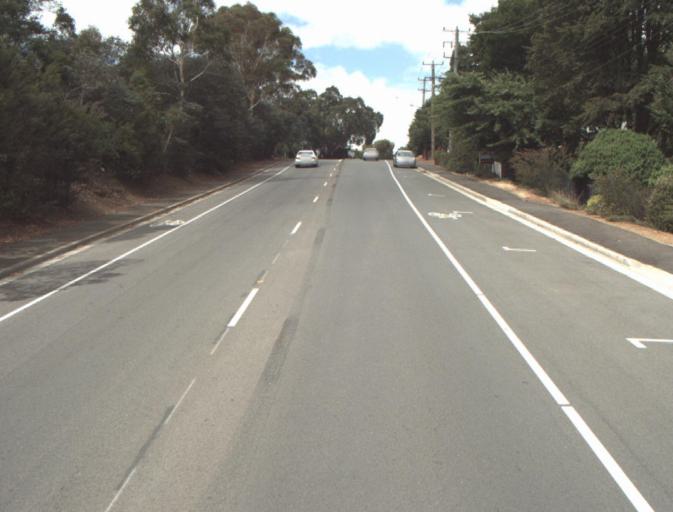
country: AU
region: Tasmania
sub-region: Launceston
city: Newstead
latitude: -41.4531
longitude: 147.1742
